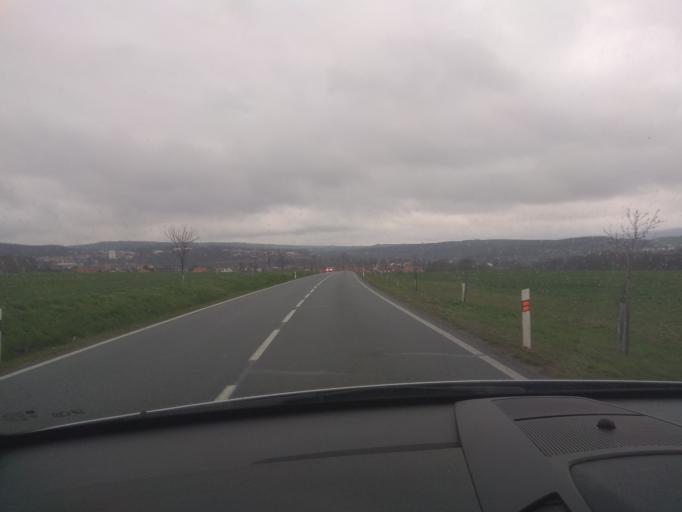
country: CZ
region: South Moravian
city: Zastavka
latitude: 49.1779
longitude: 16.3591
